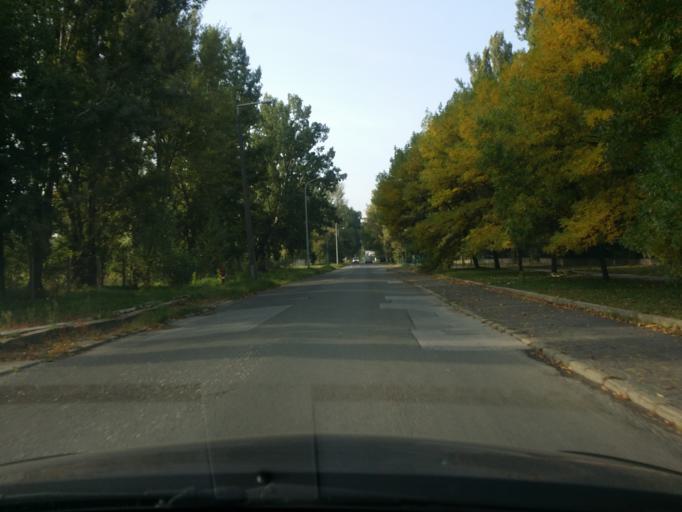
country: HU
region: Budapest
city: Budapest XIII. keruelet
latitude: 47.5445
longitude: 19.0681
